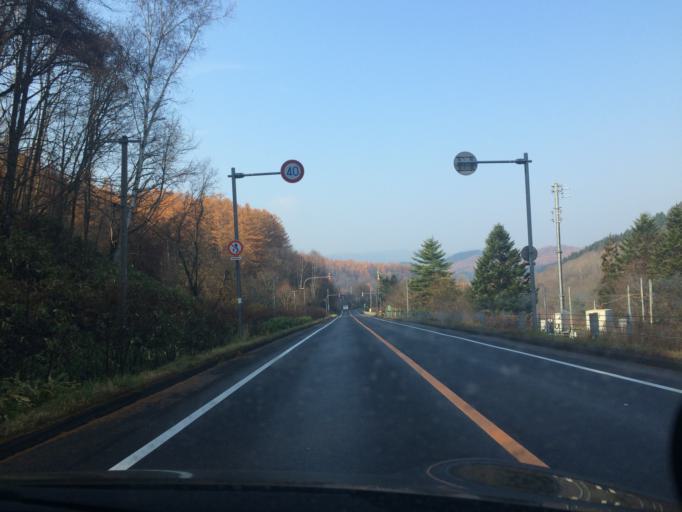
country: JP
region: Hokkaido
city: Iwamizawa
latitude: 42.9289
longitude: 142.1053
